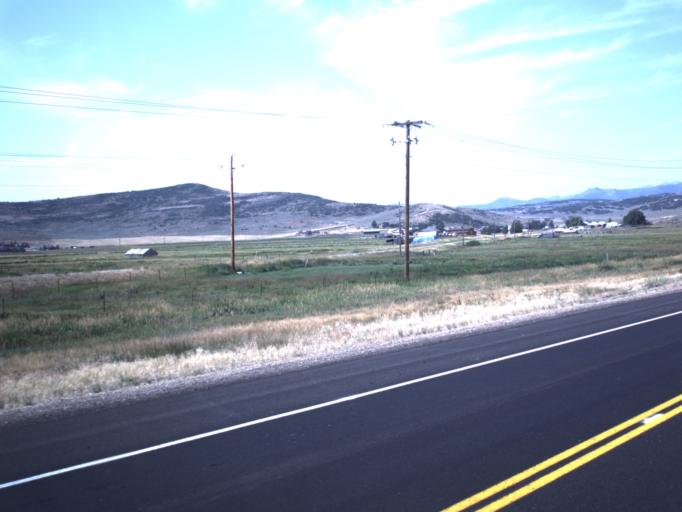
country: US
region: Utah
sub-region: Summit County
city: Kamas
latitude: 40.6400
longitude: -111.3037
